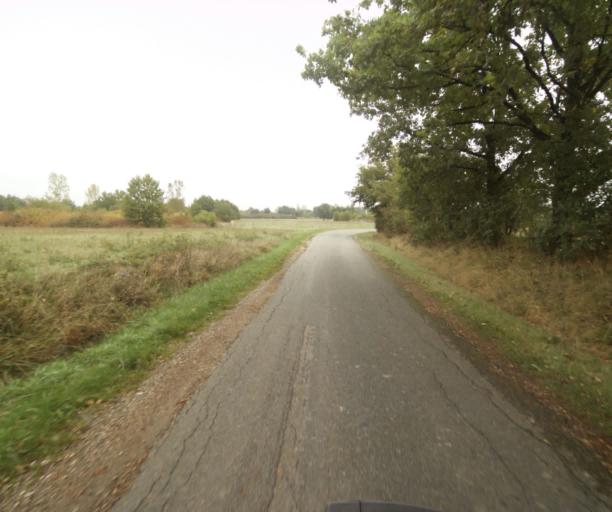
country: FR
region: Midi-Pyrenees
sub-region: Departement du Tarn-et-Garonne
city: Orgueil
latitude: 43.9039
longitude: 1.3959
